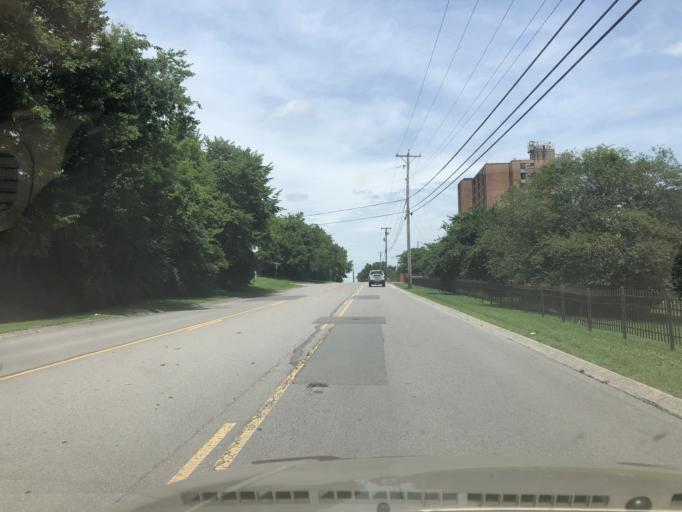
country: US
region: Tennessee
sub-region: Davidson County
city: Lakewood
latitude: 36.2535
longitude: -86.6720
